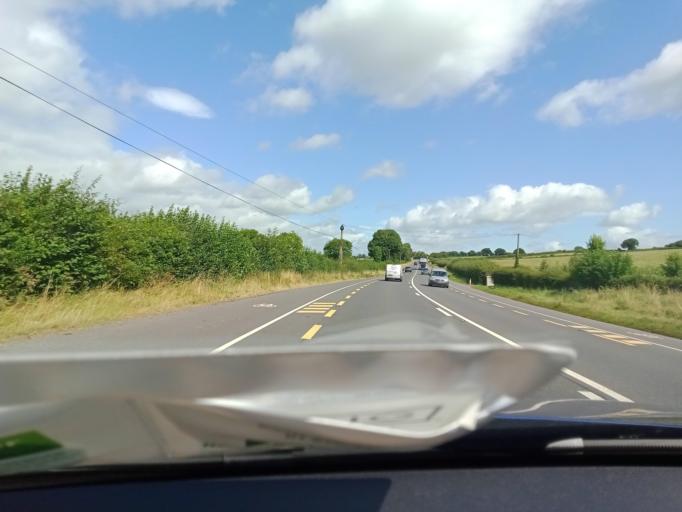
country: IE
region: Leinster
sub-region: Laois
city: Abbeyleix
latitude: 52.8653
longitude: -7.3682
